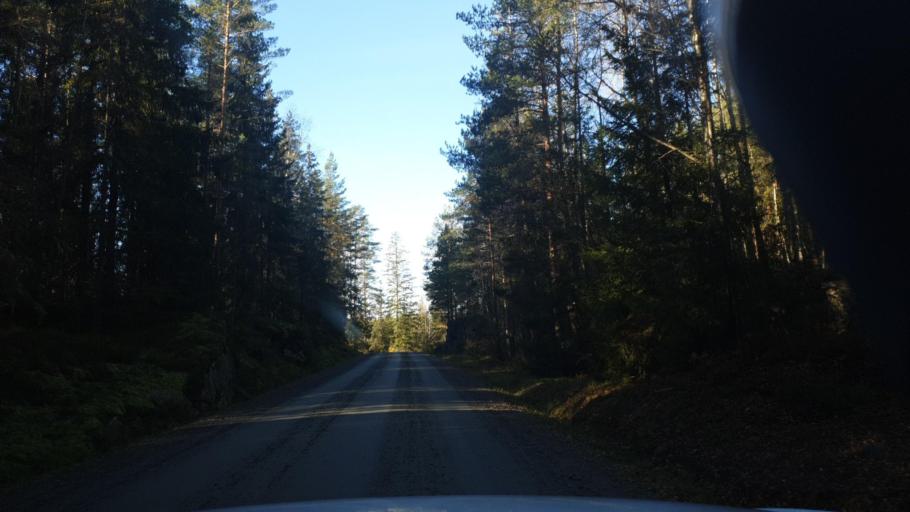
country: SE
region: Vaermland
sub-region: Karlstads Kommun
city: Edsvalla
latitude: 59.4414
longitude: 13.1876
